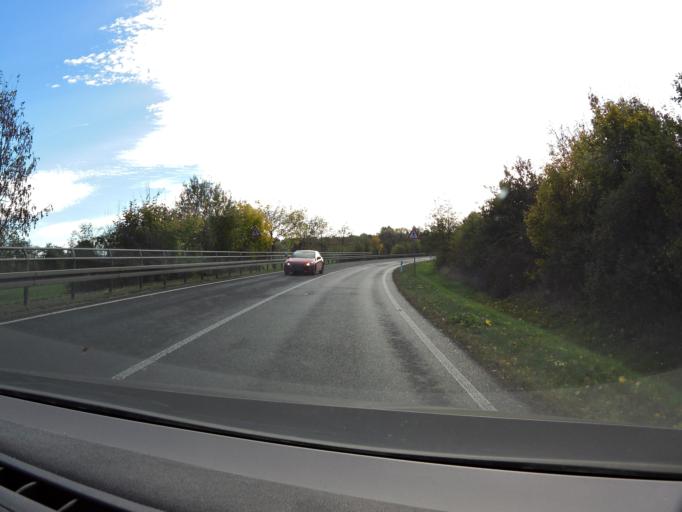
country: DE
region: Thuringia
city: Luisenthal
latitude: 50.8109
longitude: 10.7436
